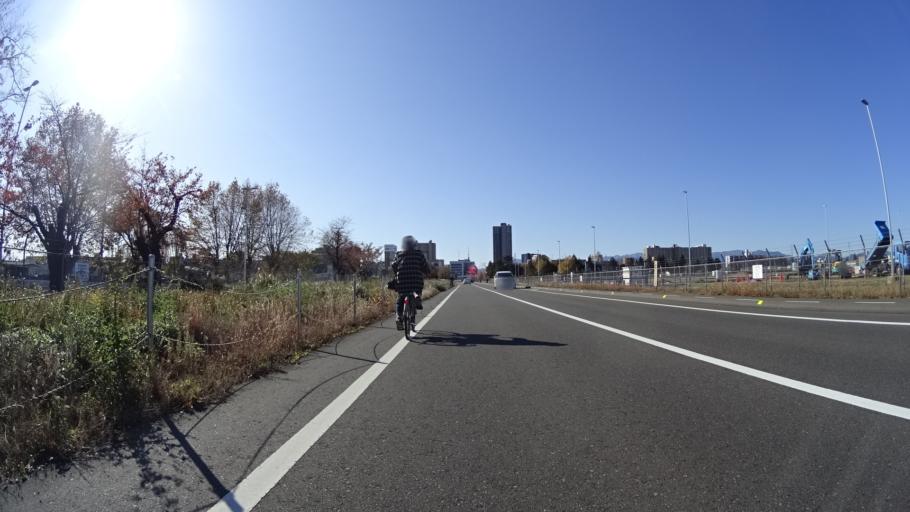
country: JP
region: Tokyo
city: Hachioji
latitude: 35.5853
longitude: 139.3753
